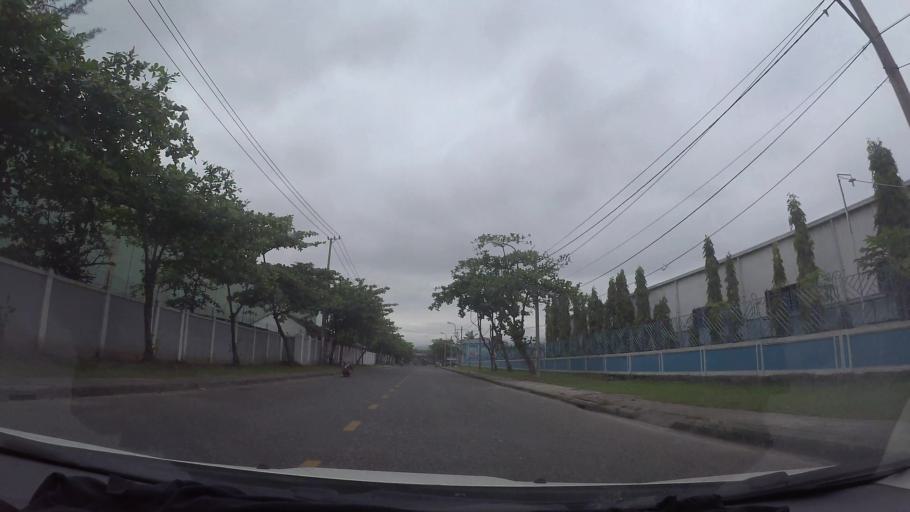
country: VN
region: Da Nang
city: Lien Chieu
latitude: 16.0819
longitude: 108.1415
